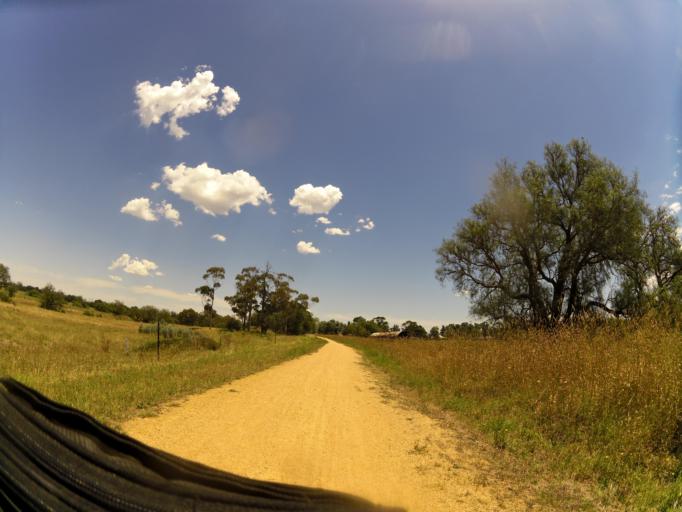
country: AU
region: Victoria
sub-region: Wellington
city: Heyfield
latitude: -37.9649
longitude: 146.8958
